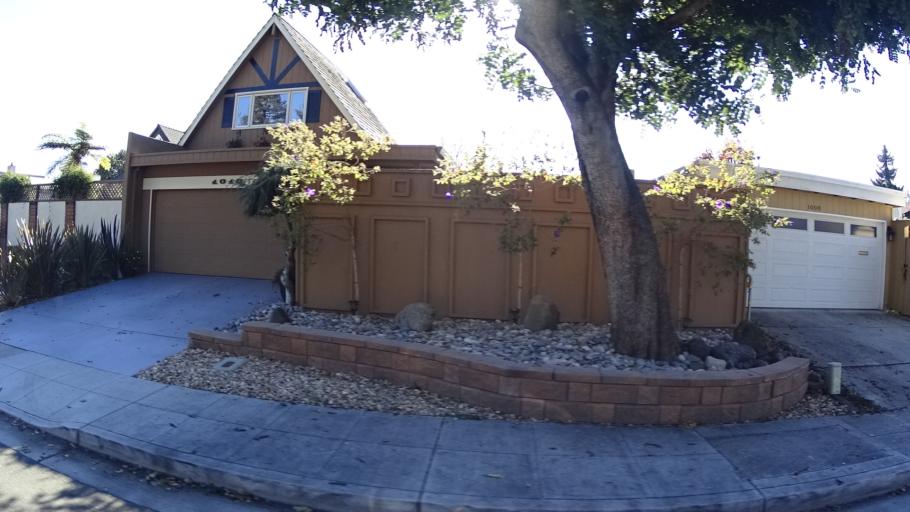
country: US
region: California
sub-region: Santa Clara County
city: Sunnyvale
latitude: 37.3700
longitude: -122.0061
